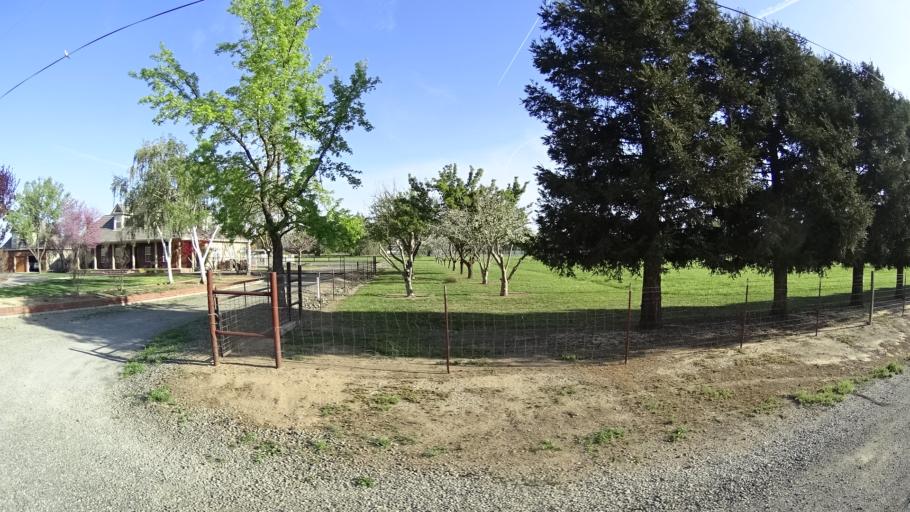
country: US
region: California
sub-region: Glenn County
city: Orland
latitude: 39.7332
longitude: -122.2183
